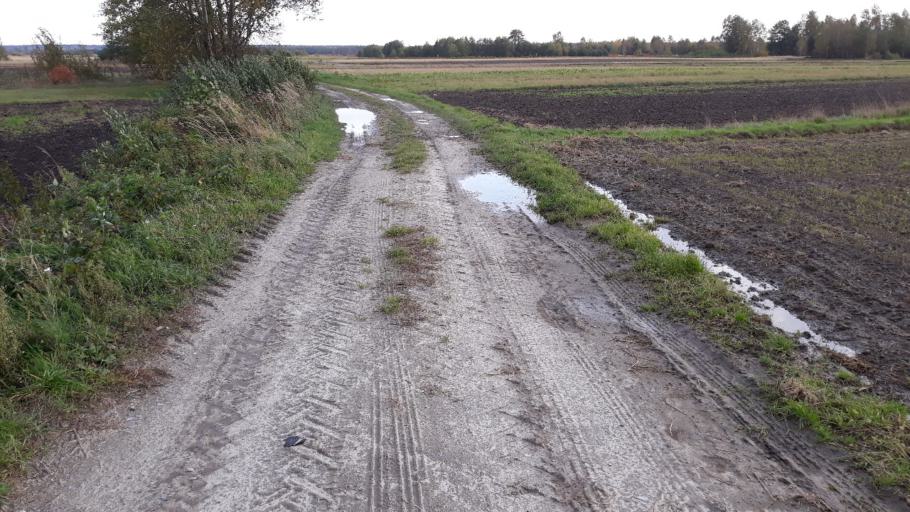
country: PL
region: Lublin Voivodeship
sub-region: Powiat janowski
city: Dzwola
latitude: 50.6648
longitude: 22.5790
